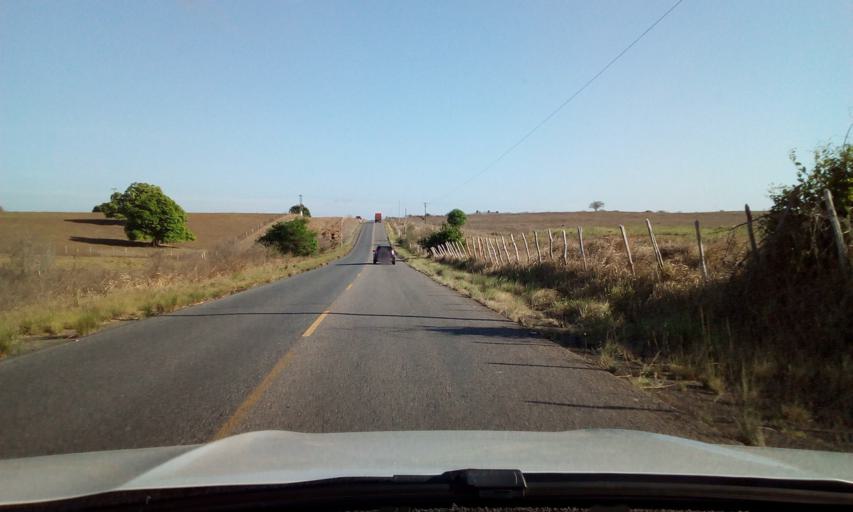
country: BR
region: Paraiba
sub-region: Mulungu
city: Mulungu
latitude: -6.9921
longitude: -35.3858
